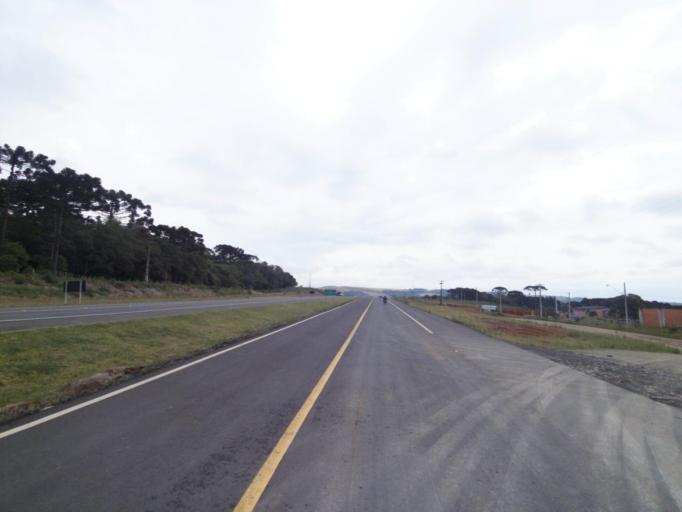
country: BR
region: Parana
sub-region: Irati
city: Irati
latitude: -25.4568
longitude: -50.6092
